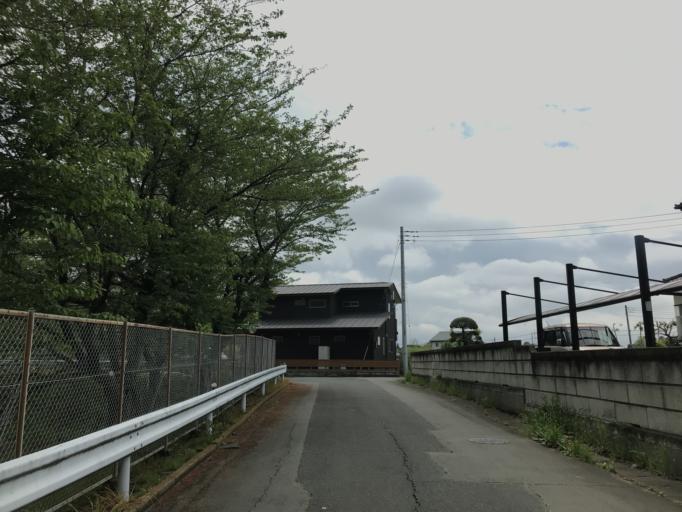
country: JP
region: Ibaraki
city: Moriya
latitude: 35.9526
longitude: 139.9591
